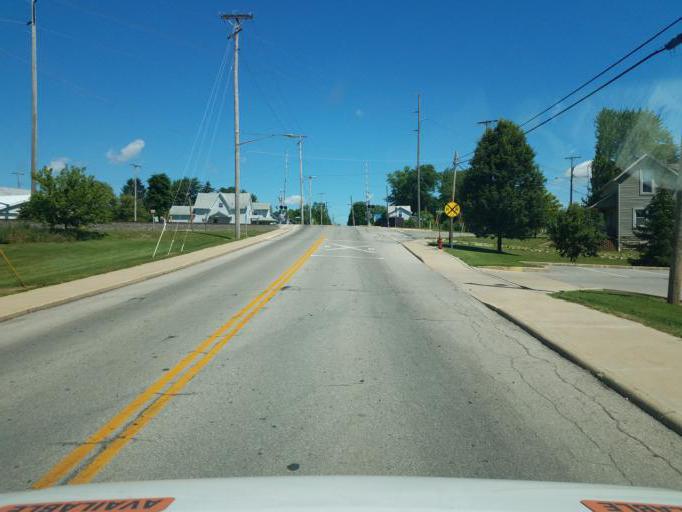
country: US
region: Ohio
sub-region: Morrow County
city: Cardington
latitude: 40.5018
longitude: -82.8947
